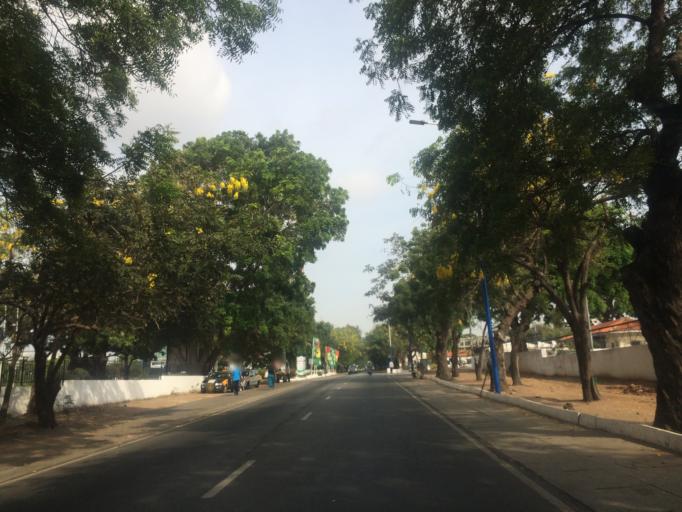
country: GH
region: Greater Accra
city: Accra
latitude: 5.5545
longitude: -0.1917
